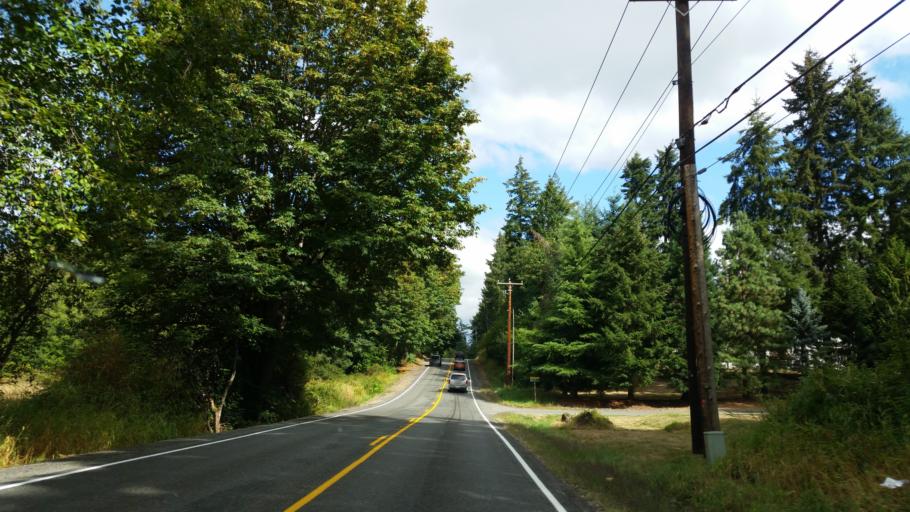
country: US
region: Washington
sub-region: Pierce County
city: Bonney Lake
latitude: 47.2467
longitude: -122.1571
